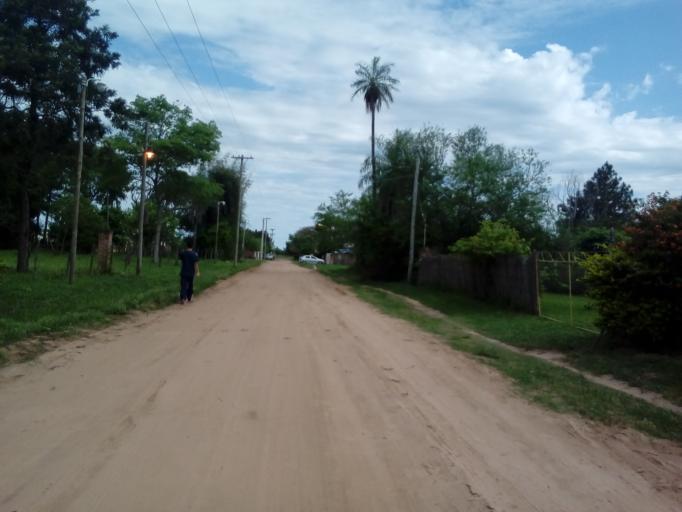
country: AR
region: Corrientes
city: San Luis del Palmar
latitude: -27.4607
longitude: -58.6526
